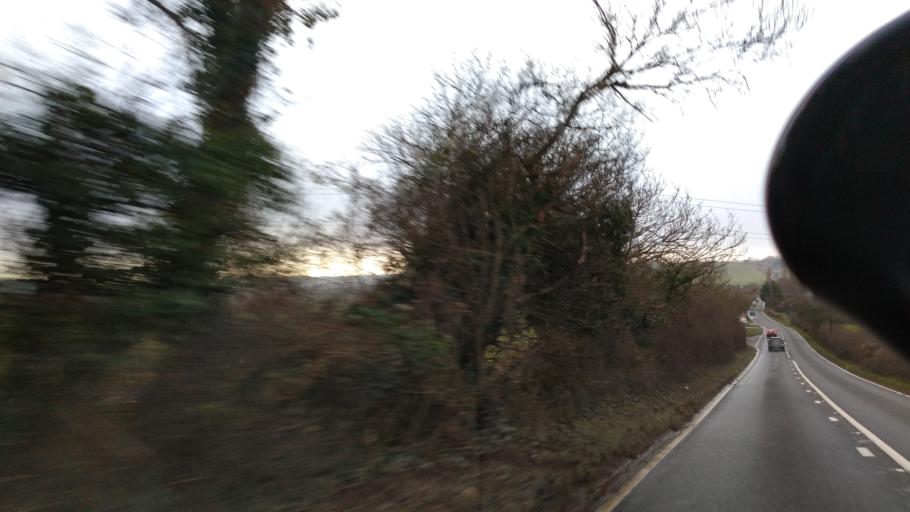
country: GB
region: England
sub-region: Somerset
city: Shepton Mallet
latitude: 51.1634
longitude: -2.5399
